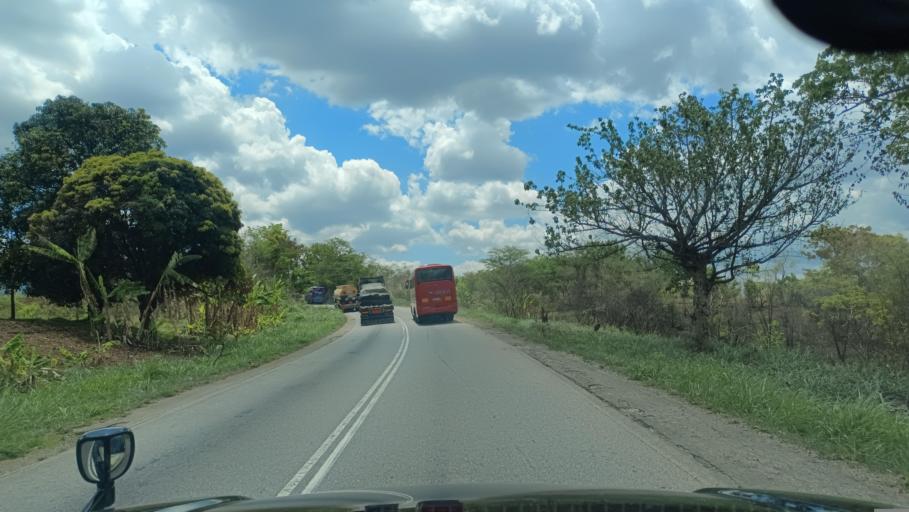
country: TZ
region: Morogoro
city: Mikumi
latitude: -7.4660
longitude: 36.9178
